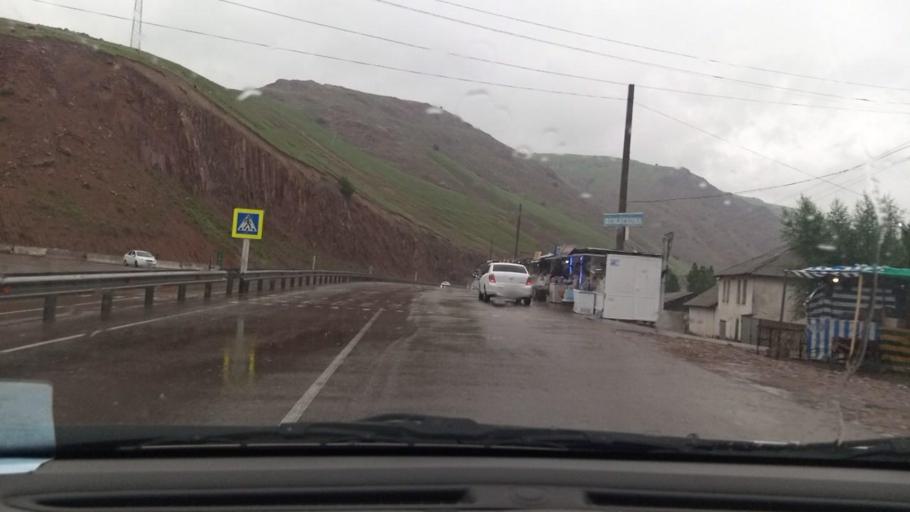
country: UZ
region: Toshkent
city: Angren
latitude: 41.1058
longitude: 70.3346
